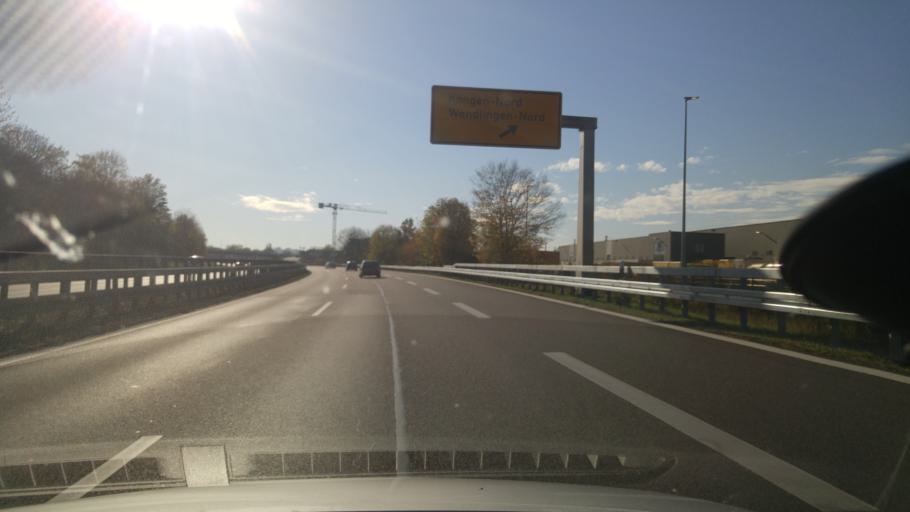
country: DE
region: Baden-Wuerttemberg
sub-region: Regierungsbezirk Stuttgart
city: Kongen
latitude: 48.6870
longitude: 9.3790
